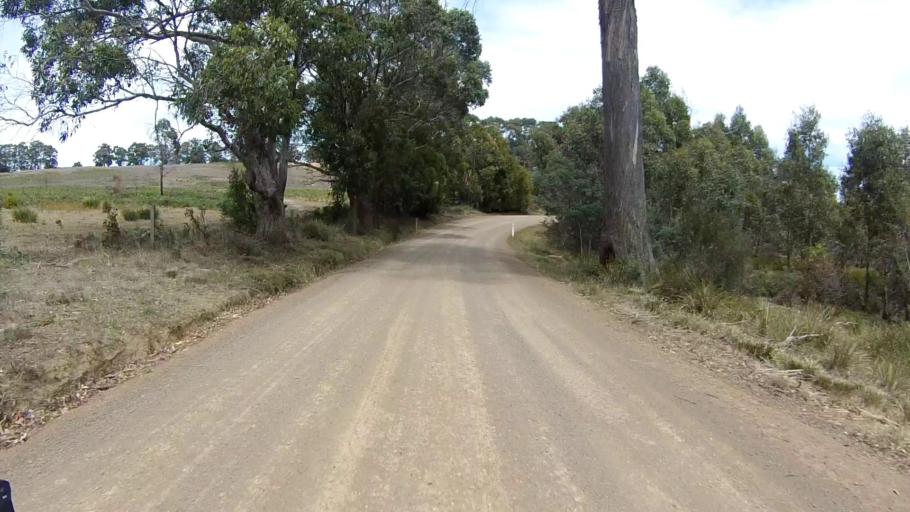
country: AU
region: Tasmania
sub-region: Sorell
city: Sorell
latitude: -42.7919
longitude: 147.6963
